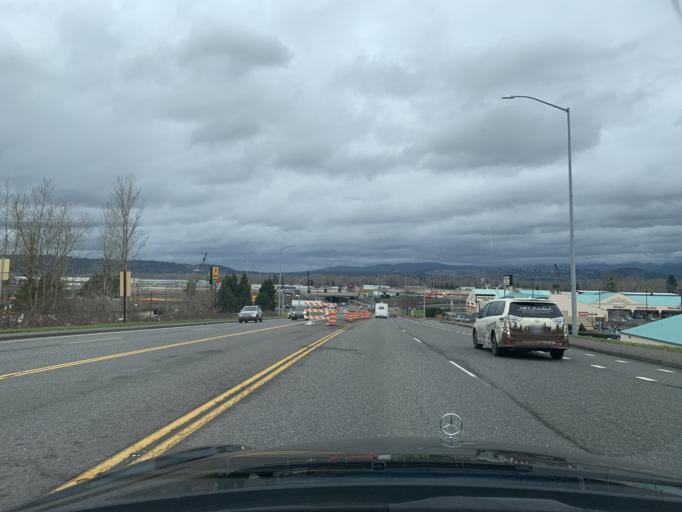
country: US
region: Oregon
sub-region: Multnomah County
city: Troutdale
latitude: 45.5420
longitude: -122.3905
